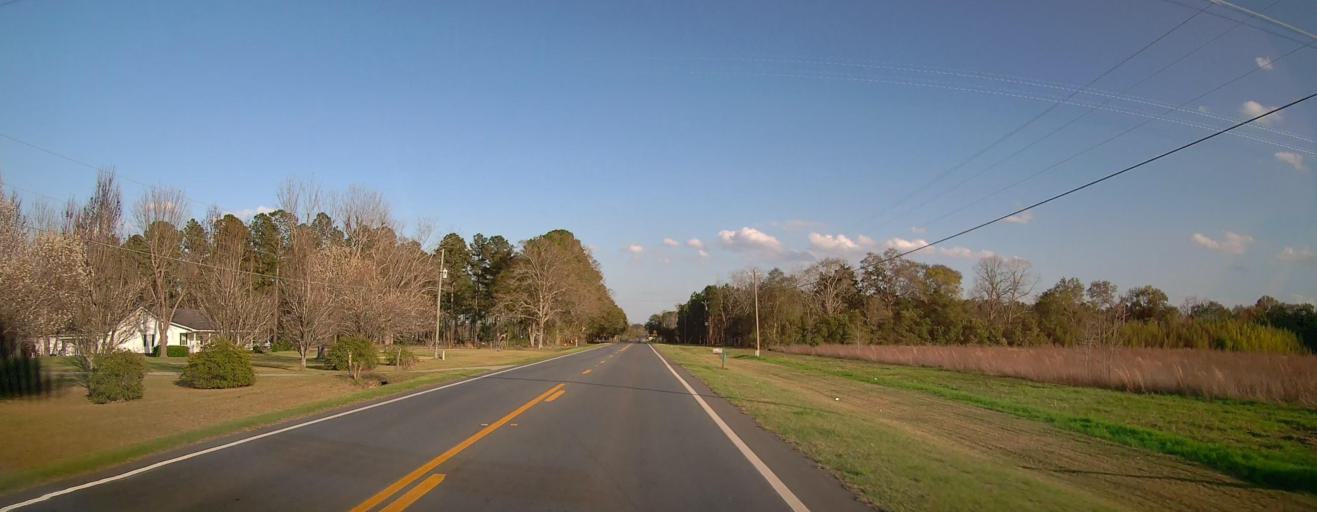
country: US
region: Georgia
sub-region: Evans County
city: Claxton
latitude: 32.1564
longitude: -81.8564
